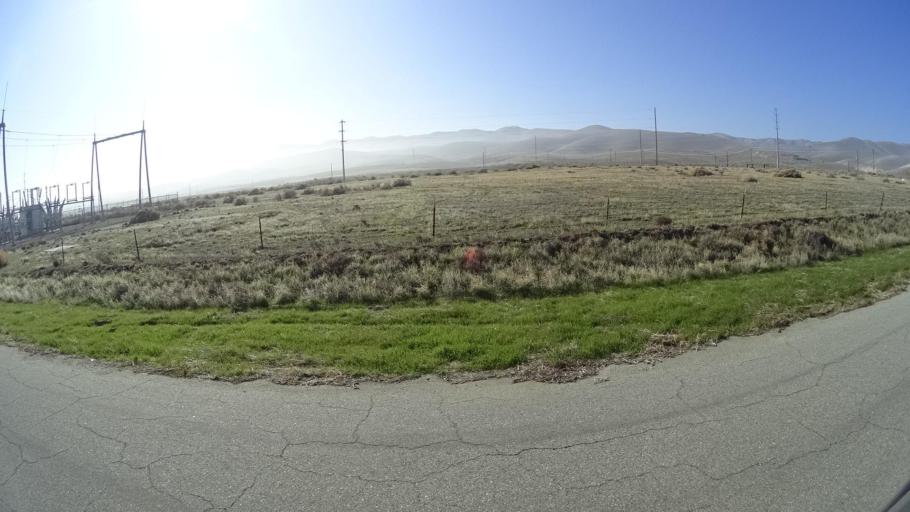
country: US
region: California
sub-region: Kern County
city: Taft Heights
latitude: 35.2269
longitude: -119.6315
